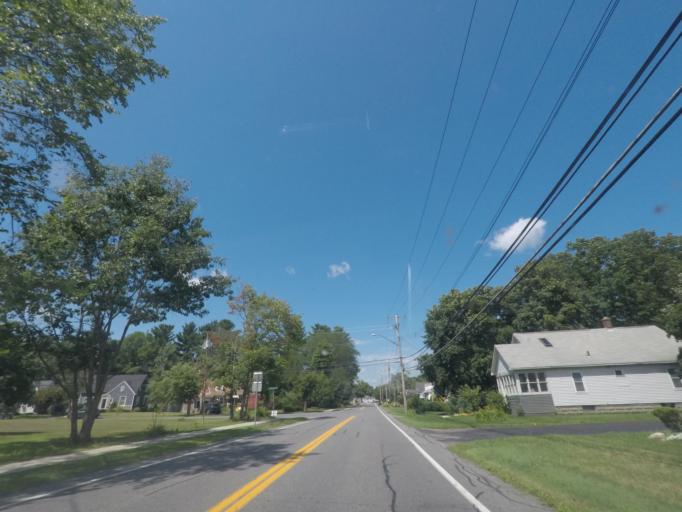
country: US
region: New York
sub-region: Schenectady County
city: Rotterdam
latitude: 42.7775
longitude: -73.9583
